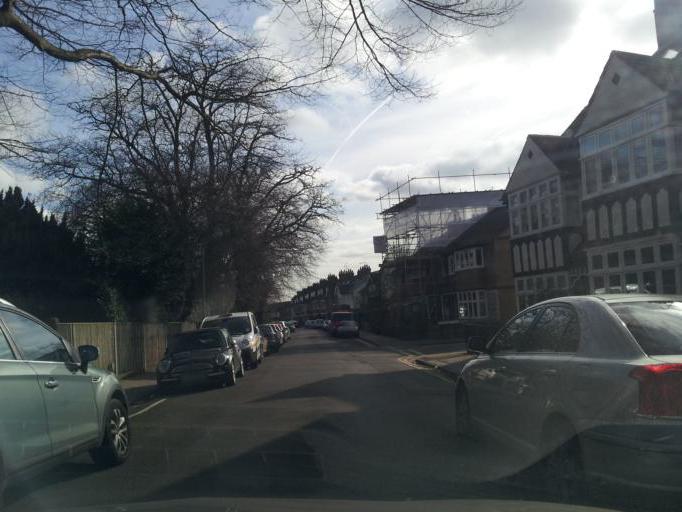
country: GB
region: England
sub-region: Hertfordshire
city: St Albans
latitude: 51.7548
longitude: -0.3193
